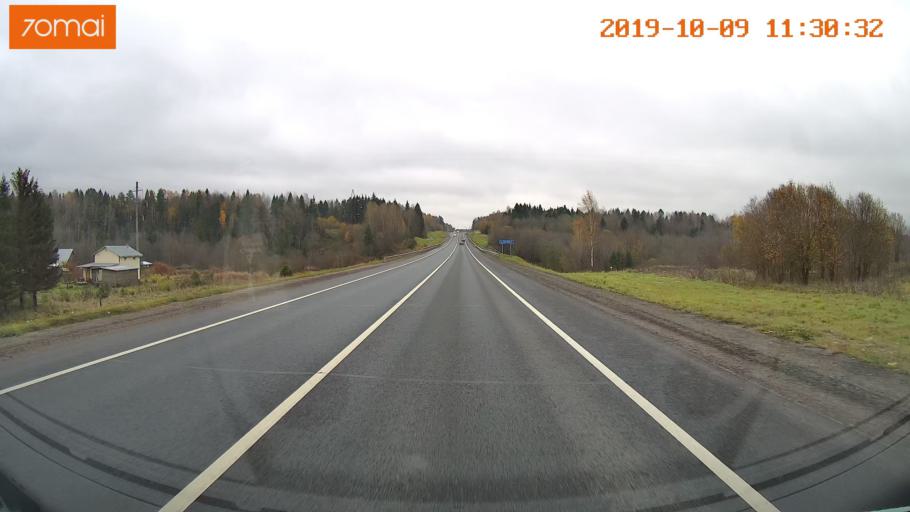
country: RU
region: Vologda
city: Gryazovets
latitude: 59.0530
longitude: 40.0772
